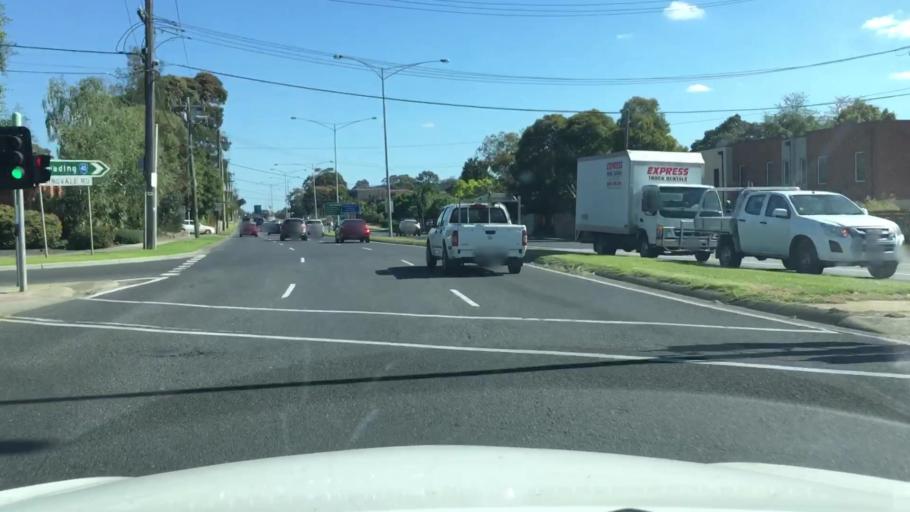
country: AU
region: Victoria
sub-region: Manningham
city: Donvale
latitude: -37.7966
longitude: 145.1791
